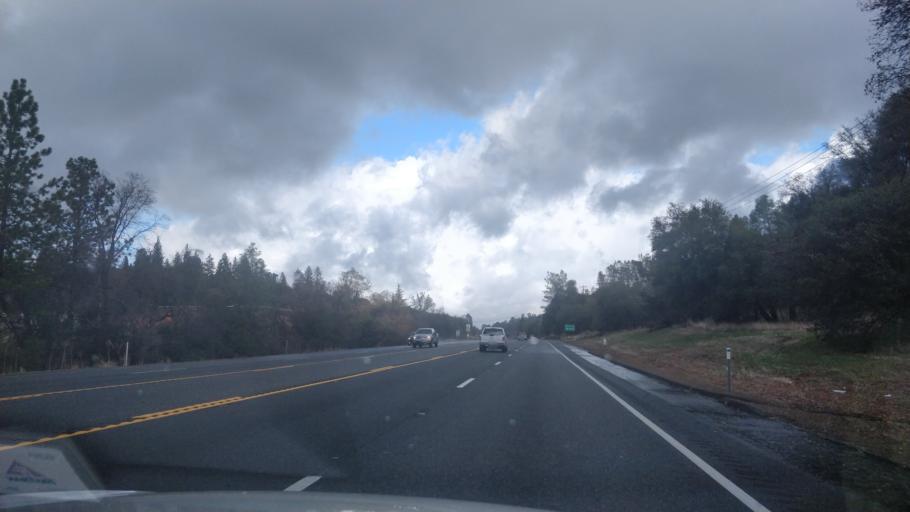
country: US
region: California
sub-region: Nevada County
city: Lake of the Pines
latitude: 39.0320
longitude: -121.0970
